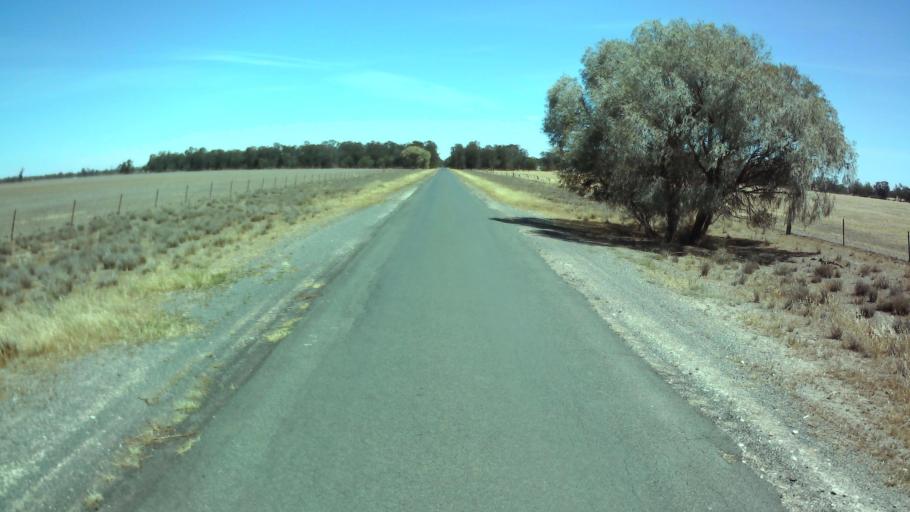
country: AU
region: New South Wales
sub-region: Weddin
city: Grenfell
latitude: -33.8634
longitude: 147.6933
